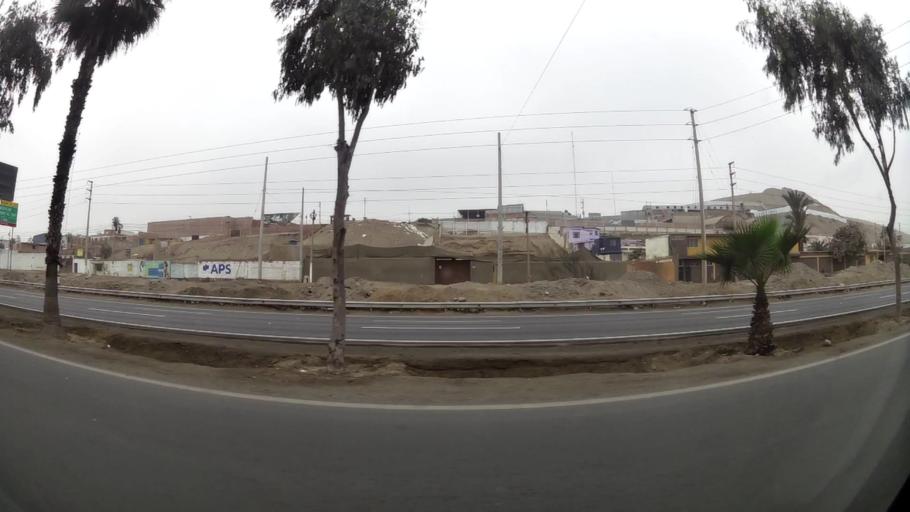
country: PE
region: Lima
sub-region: Lima
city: Surco
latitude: -12.2293
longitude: -76.9680
